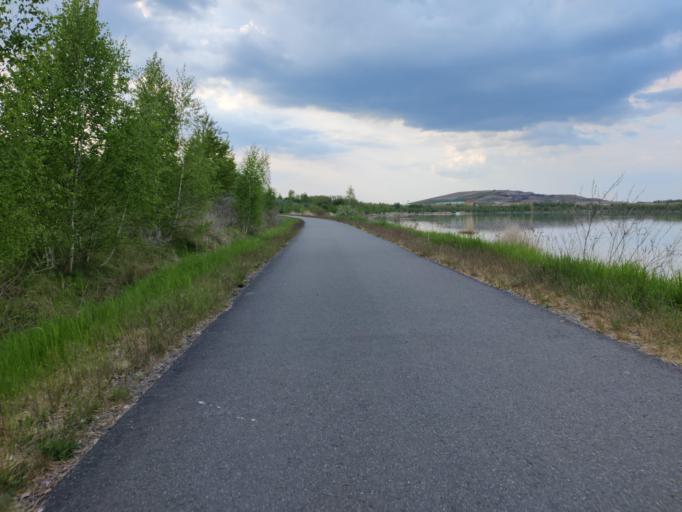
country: DE
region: Saxony
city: Rotha
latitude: 51.2239
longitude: 12.4292
